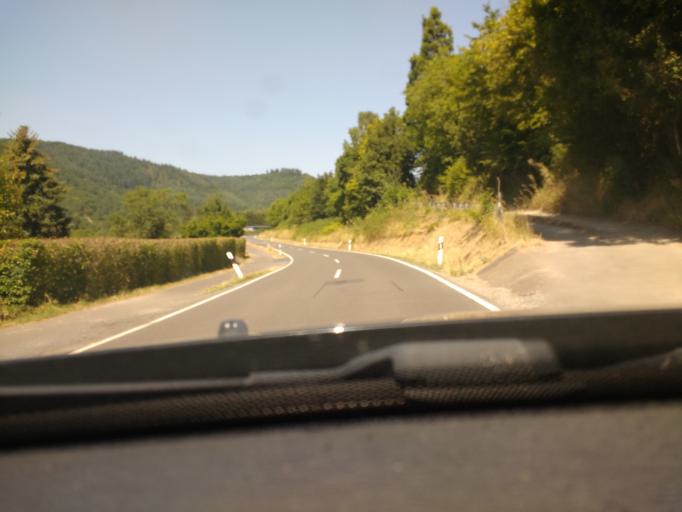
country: DE
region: Rheinland-Pfalz
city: Wittlich
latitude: 49.9987
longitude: 6.8821
